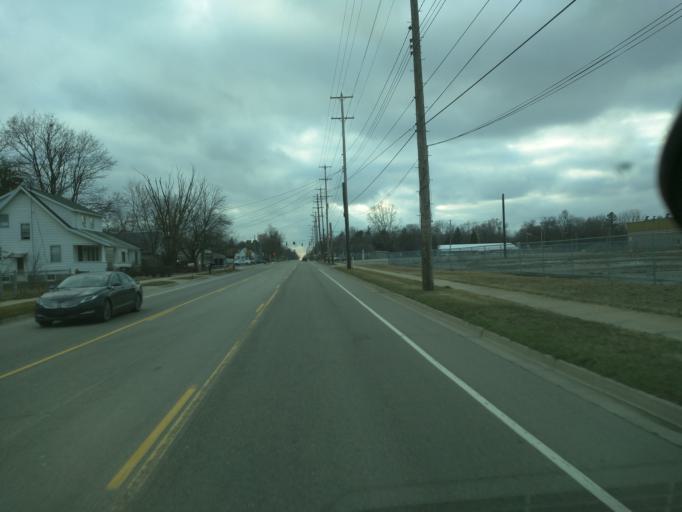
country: US
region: Michigan
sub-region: Ingham County
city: Edgemont Park
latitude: 42.7338
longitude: -84.5853
